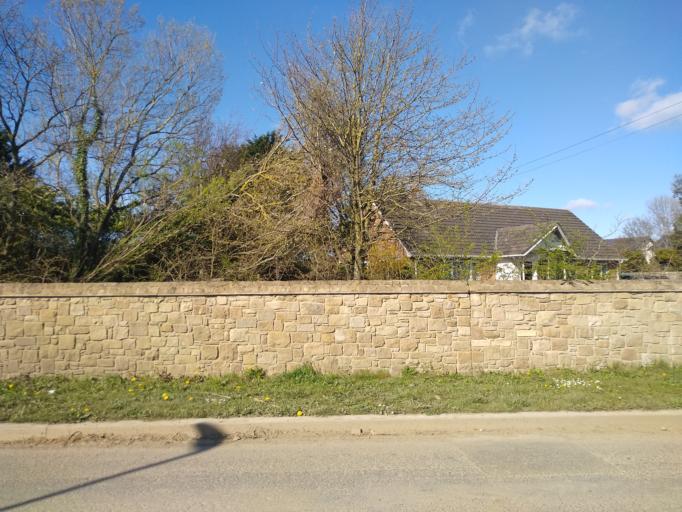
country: IE
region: Leinster
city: Malahide
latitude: 53.4333
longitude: -6.1674
